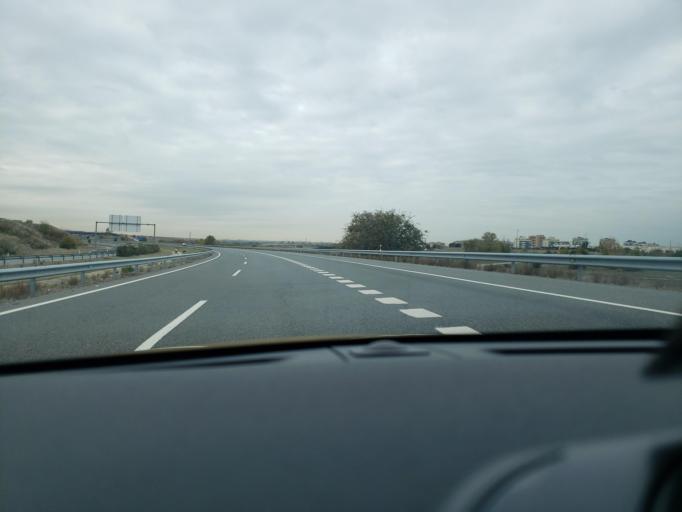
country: ES
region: Madrid
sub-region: Provincia de Madrid
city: Mostoles
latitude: 40.3057
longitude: -3.8430
